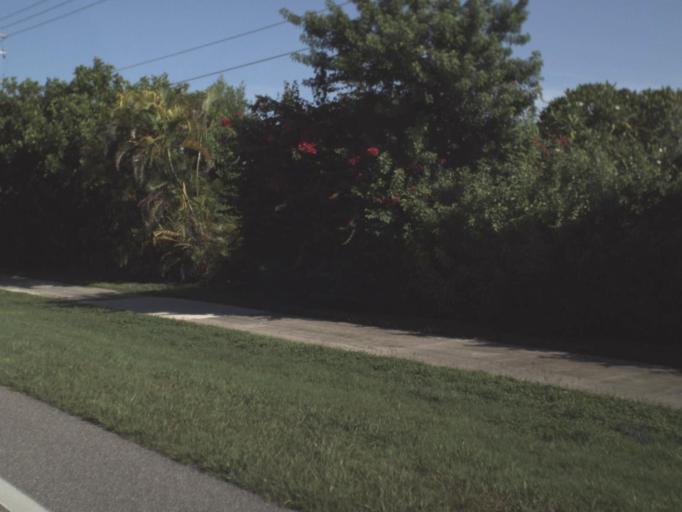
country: US
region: Florida
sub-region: Sarasota County
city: Siesta Key
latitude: 27.3488
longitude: -82.6060
